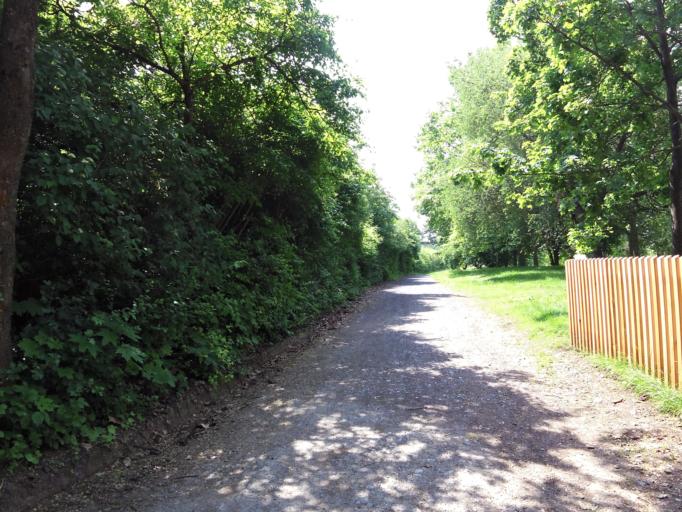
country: DE
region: Bavaria
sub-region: Regierungsbezirk Unterfranken
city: Wuerzburg
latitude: 49.7841
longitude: 9.9619
